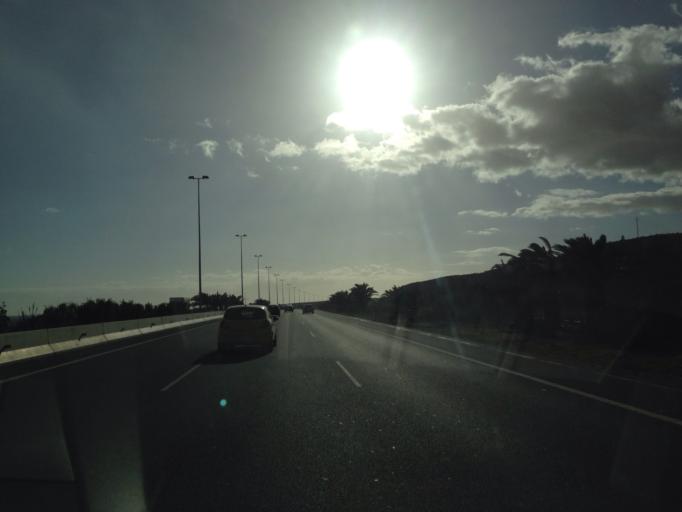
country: ES
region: Canary Islands
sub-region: Provincia de Las Palmas
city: Playa del Ingles
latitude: 27.7974
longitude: -15.4897
